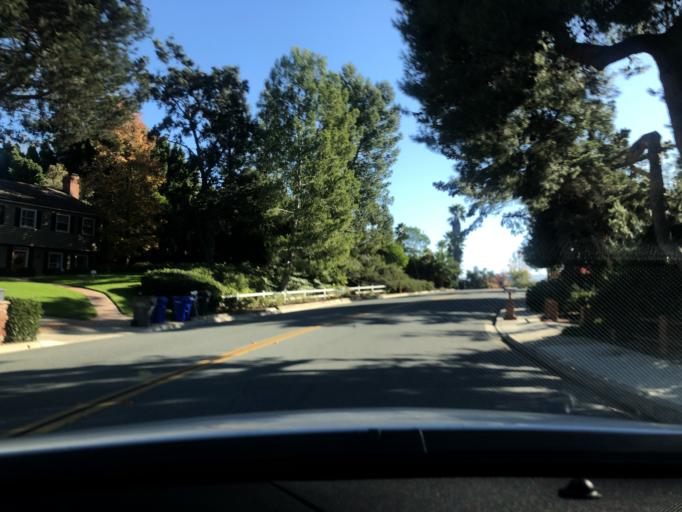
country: US
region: California
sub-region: San Diego County
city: Rancho San Diego
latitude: 32.7697
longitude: -116.9447
